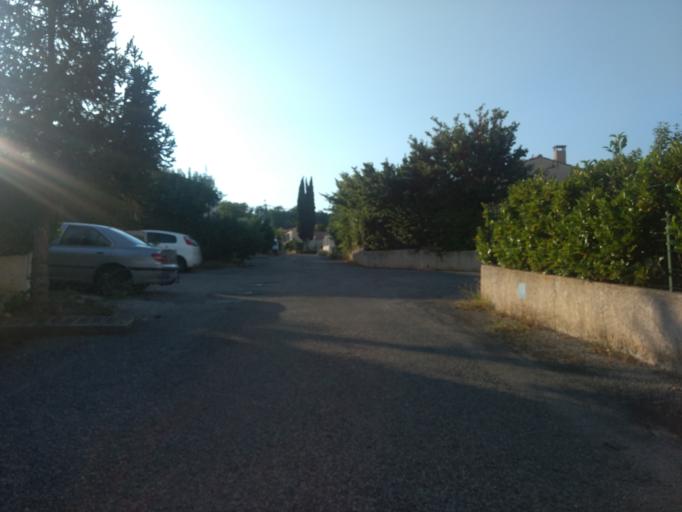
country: FR
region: Provence-Alpes-Cote d'Azur
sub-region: Departement des Alpes-de-Haute-Provence
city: Manosque
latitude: 43.8219
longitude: 5.7752
